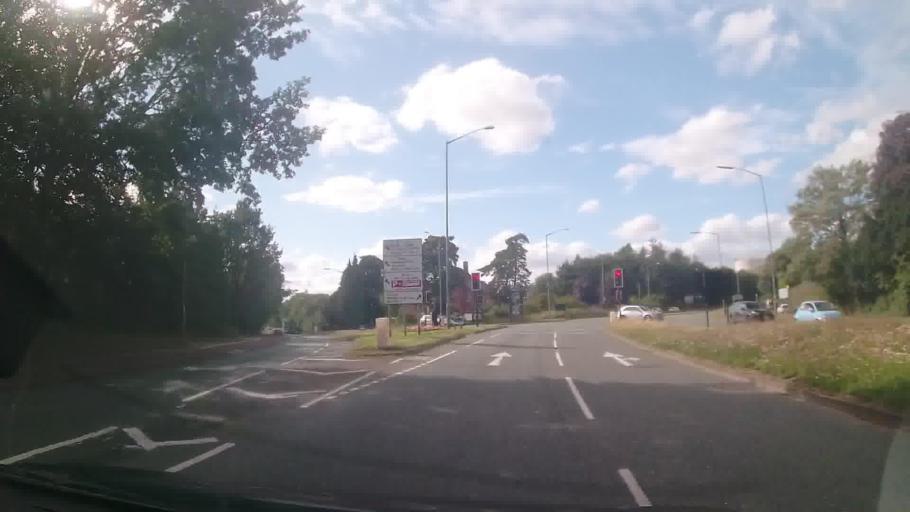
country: GB
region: England
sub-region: Shropshire
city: Bicton
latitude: 52.7142
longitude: -2.7916
